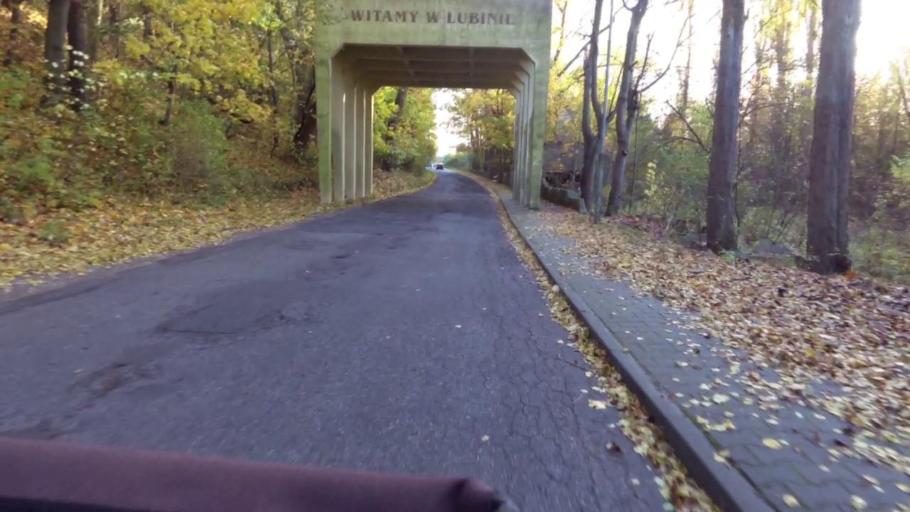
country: PL
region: West Pomeranian Voivodeship
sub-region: Powiat kamienski
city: Miedzyzdroje
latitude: 53.8757
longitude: 14.4279
